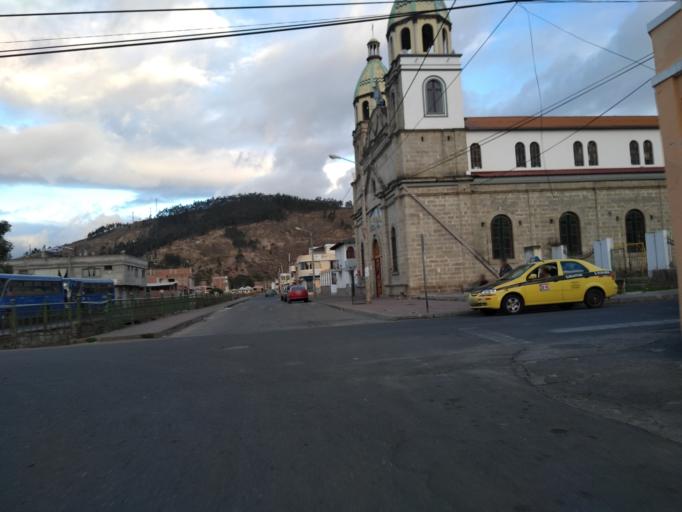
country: EC
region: Chimborazo
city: Riobamba
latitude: -1.6891
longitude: -78.6764
